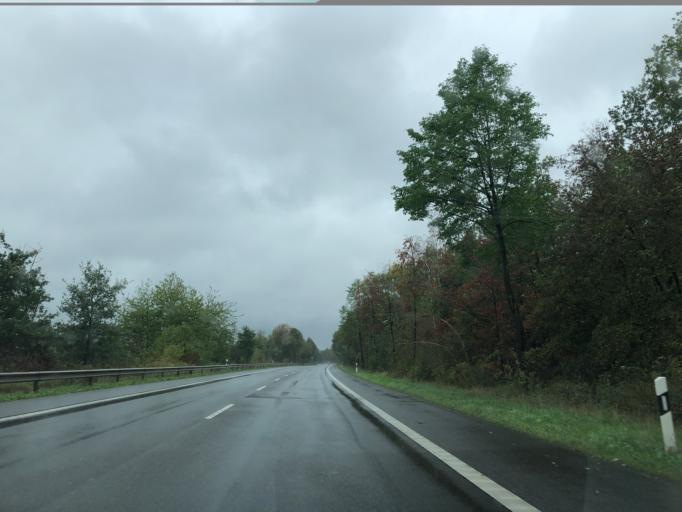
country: DE
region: North Rhine-Westphalia
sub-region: Regierungsbezirk Dusseldorf
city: Grevenbroich
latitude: 51.0741
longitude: 6.5579
